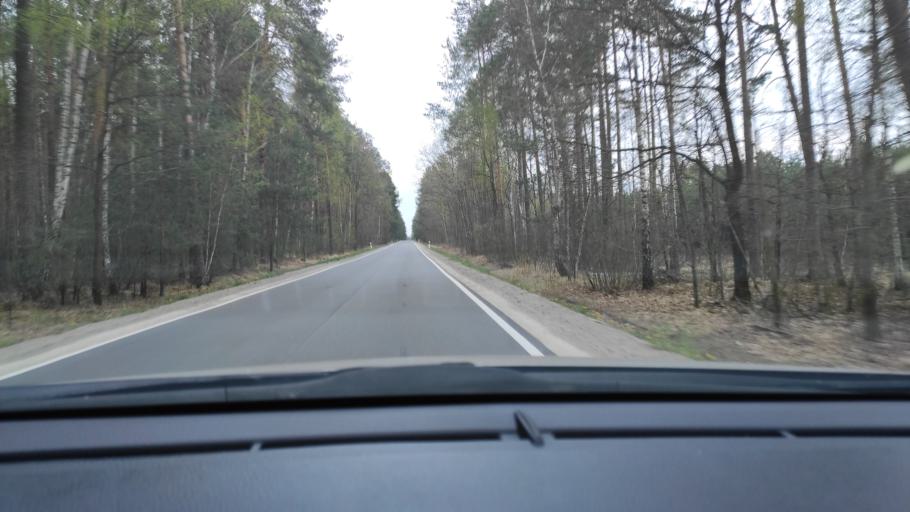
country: PL
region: Masovian Voivodeship
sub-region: Powiat zwolenski
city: Zwolen
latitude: 51.3936
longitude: 21.5456
